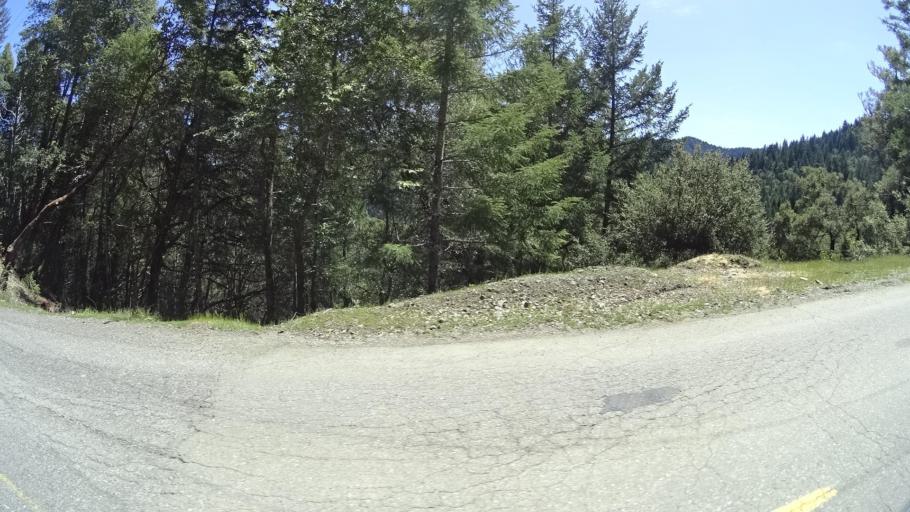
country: US
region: California
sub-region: Humboldt County
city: Rio Dell
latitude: 40.3217
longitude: -124.0574
